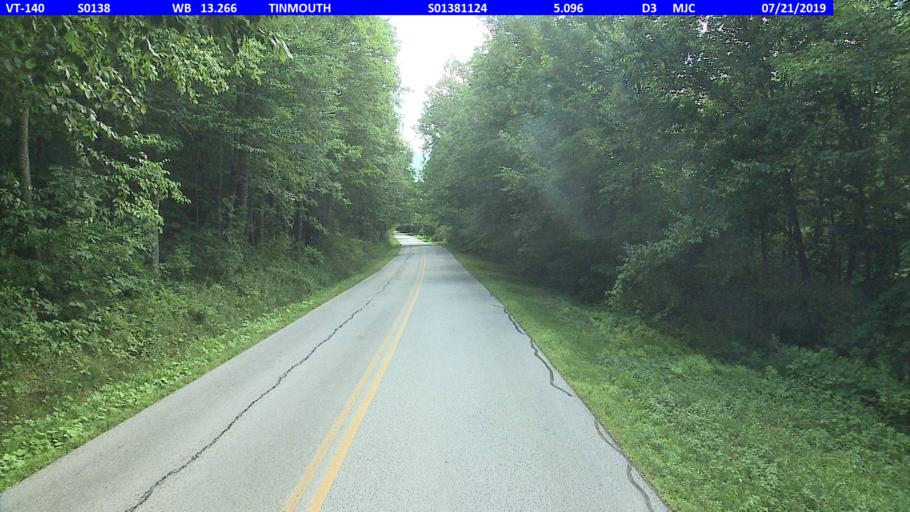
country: US
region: Vermont
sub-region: Rutland County
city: West Rutland
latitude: 43.4562
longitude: -73.0200
